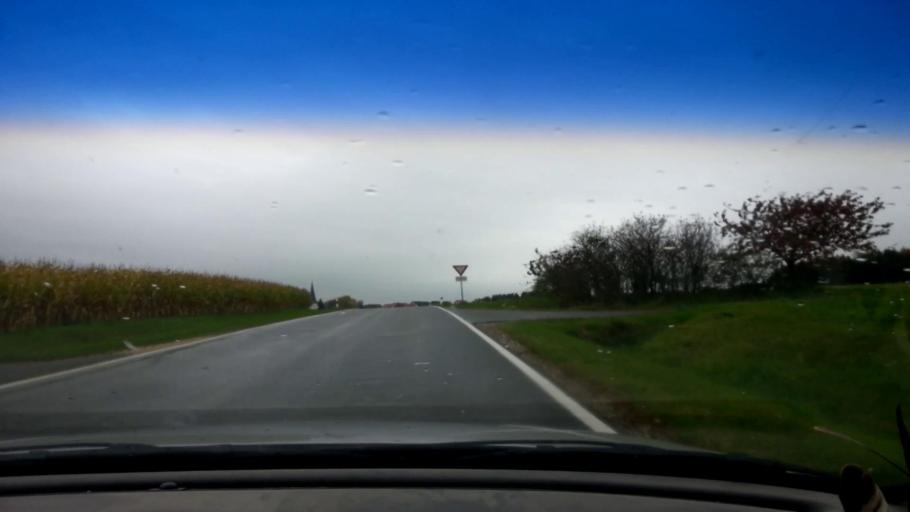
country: DE
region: Bavaria
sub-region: Upper Franconia
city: Poxdorf
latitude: 49.8752
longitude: 11.0976
